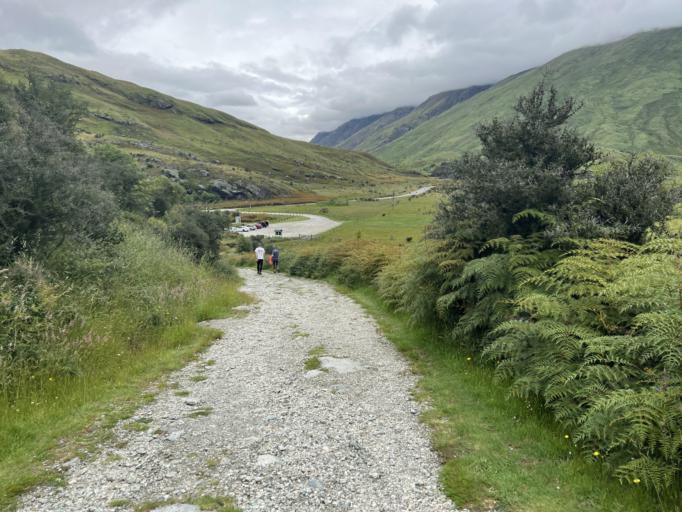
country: NZ
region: Otago
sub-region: Queenstown-Lakes District
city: Wanaka
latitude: -44.6498
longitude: 168.9597
